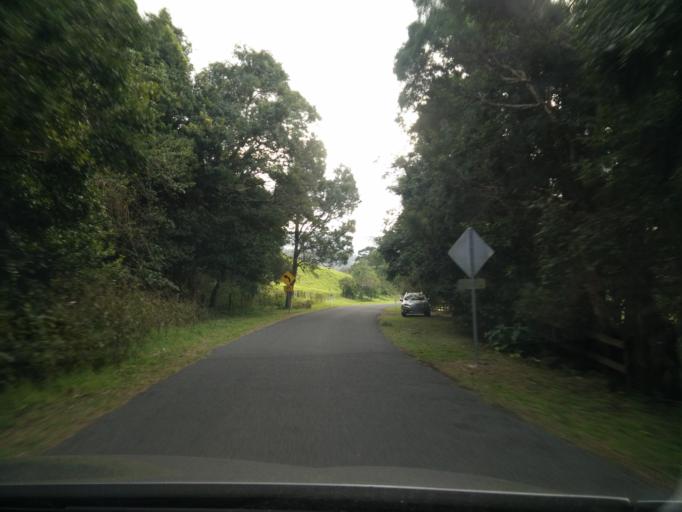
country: AU
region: New South Wales
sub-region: Kiama
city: Jamberoo
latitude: -34.6948
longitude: 150.7922
